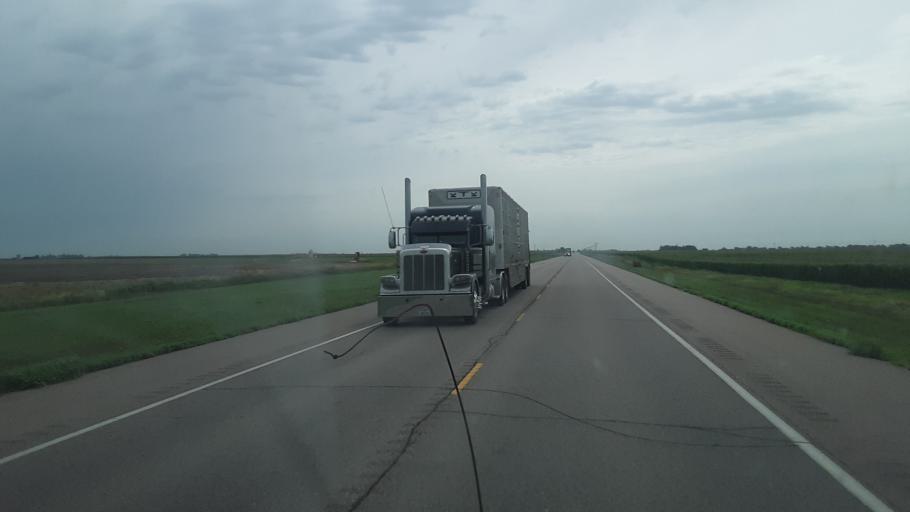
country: US
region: Kansas
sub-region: Stafford County
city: Saint John
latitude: 37.9562
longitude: -98.8843
